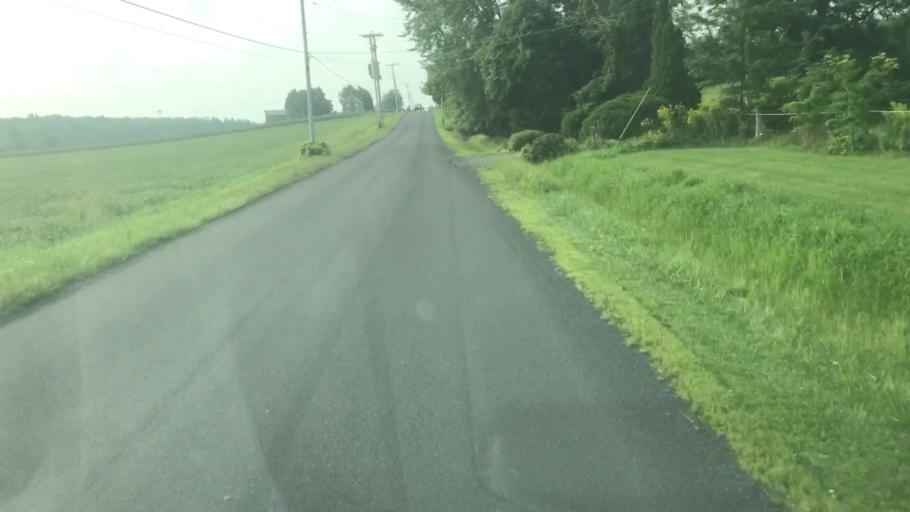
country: US
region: New York
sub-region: Onondaga County
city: Skaneateles
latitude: 42.9309
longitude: -76.4575
